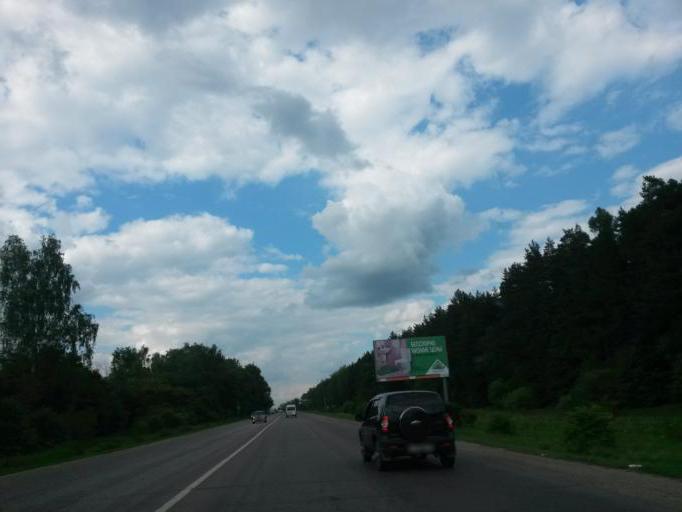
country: RU
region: Moskovskaya
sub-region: Chekhovskiy Rayon
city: Chekhov
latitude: 55.1912
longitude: 37.5024
